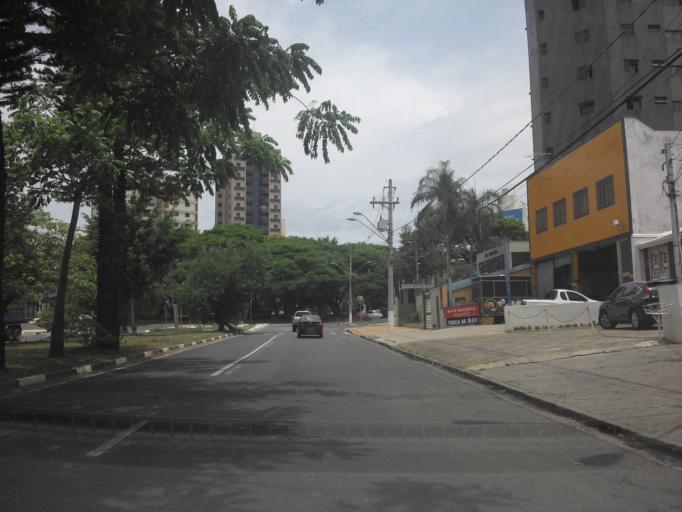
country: BR
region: Sao Paulo
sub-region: Campinas
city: Campinas
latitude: -22.9184
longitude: -47.0445
